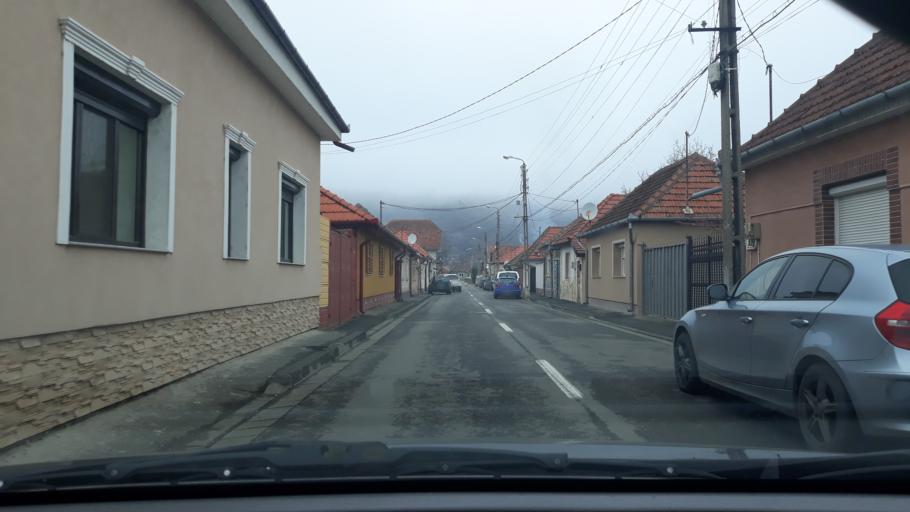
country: RO
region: Bihor
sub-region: Comuna Sanmartin
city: Sanmartin
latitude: 47.0476
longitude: 21.9725
